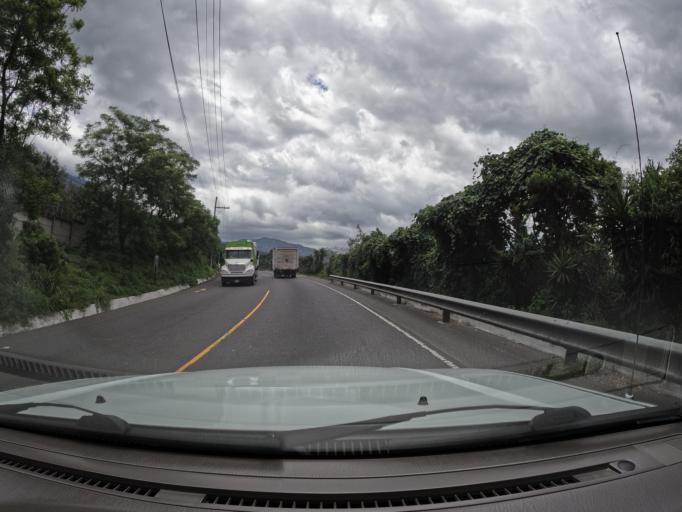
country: GT
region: Sacatepequez
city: Alotenango
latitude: 14.4841
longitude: -90.8091
